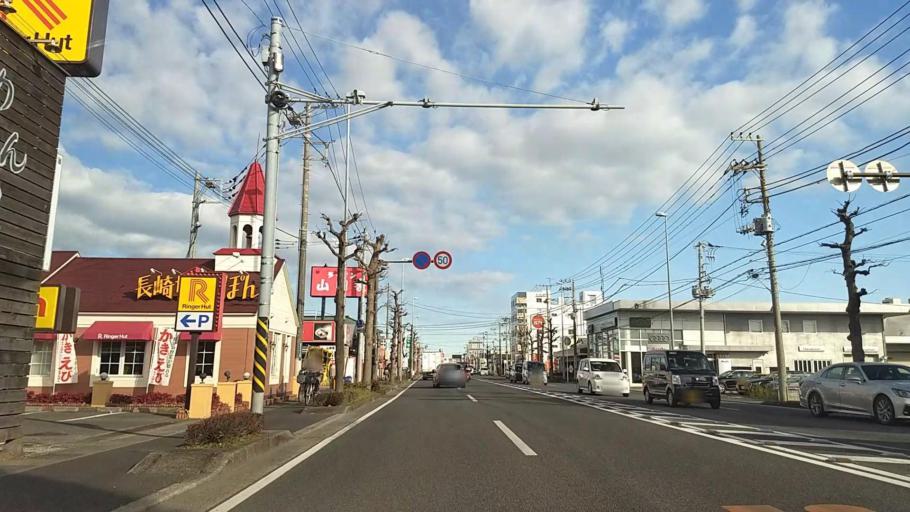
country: JP
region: Kanagawa
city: Hiratsuka
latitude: 35.3558
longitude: 139.3572
